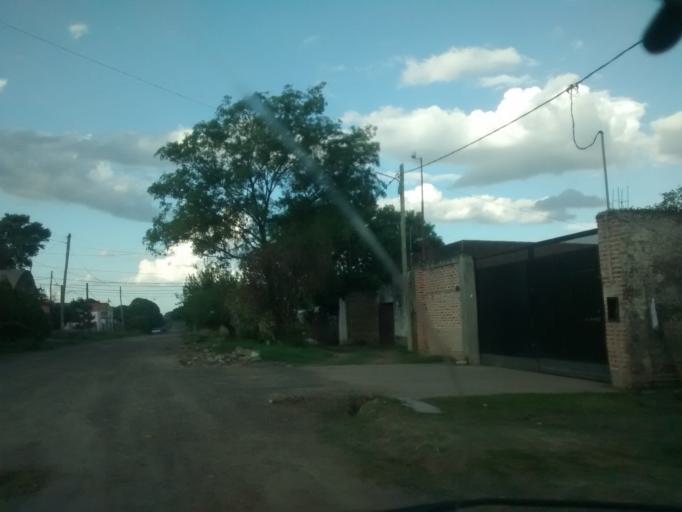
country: AR
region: Chaco
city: Fontana
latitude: -27.4398
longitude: -59.0128
